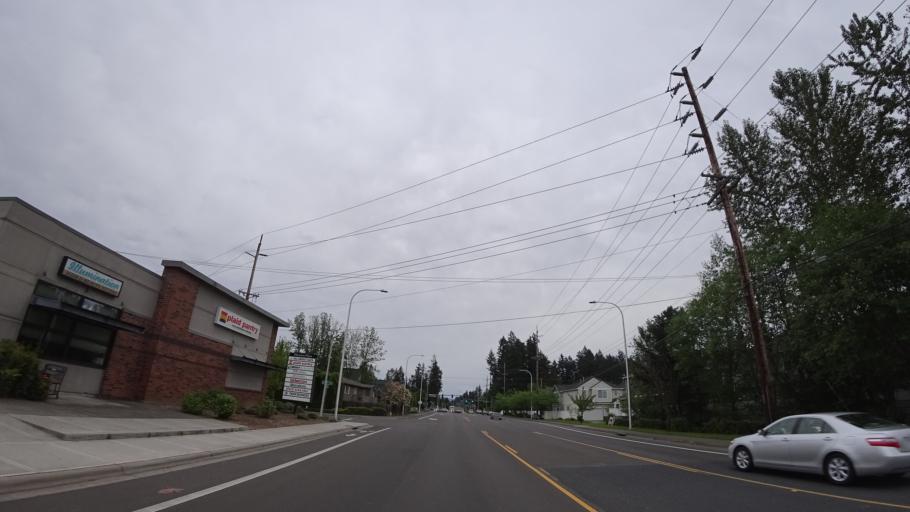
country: US
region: Oregon
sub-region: Washington County
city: Hillsboro
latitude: 45.5200
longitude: -122.9387
